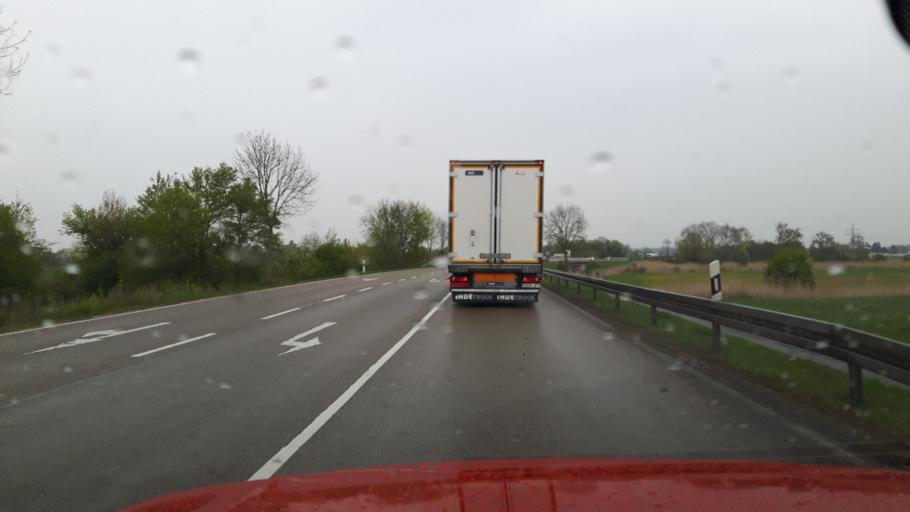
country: DE
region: Bavaria
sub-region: Regierungsbezirk Mittelfranken
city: Gunzenhausen
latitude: 49.1208
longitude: 10.7375
